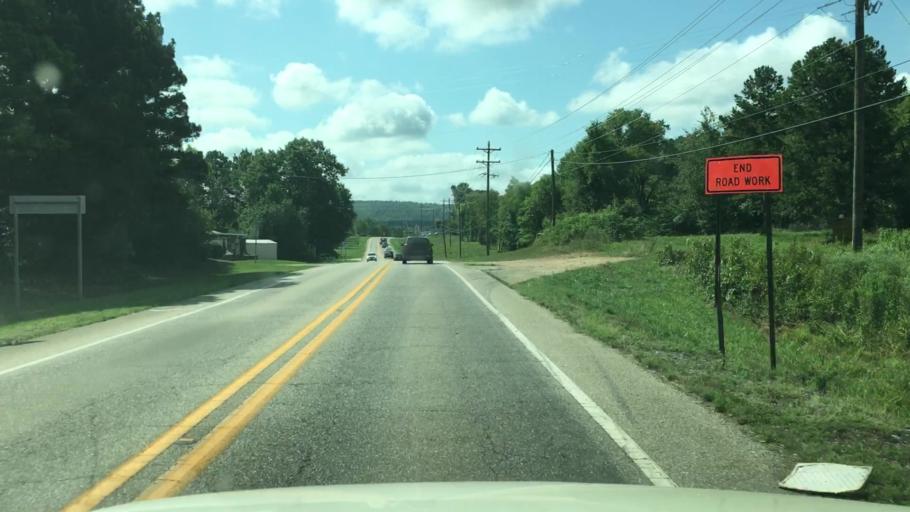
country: US
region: Arkansas
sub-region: Garland County
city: Lake Hamilton
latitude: 34.4107
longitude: -93.0935
